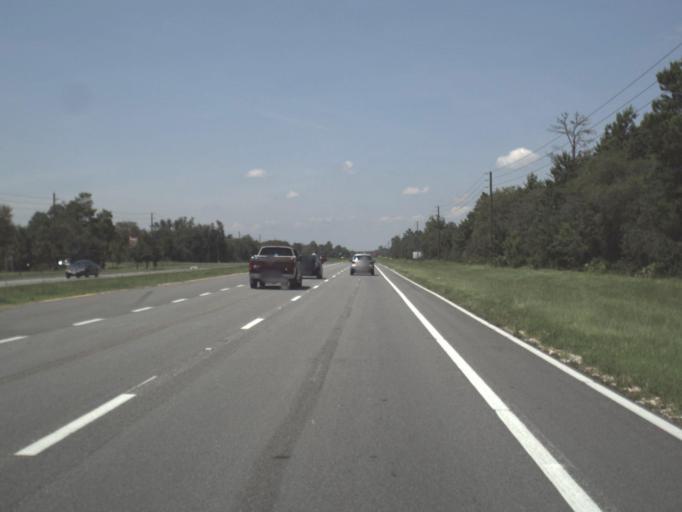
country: US
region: Florida
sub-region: Hernando County
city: North Weeki Wachee
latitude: 28.5700
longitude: -82.5582
